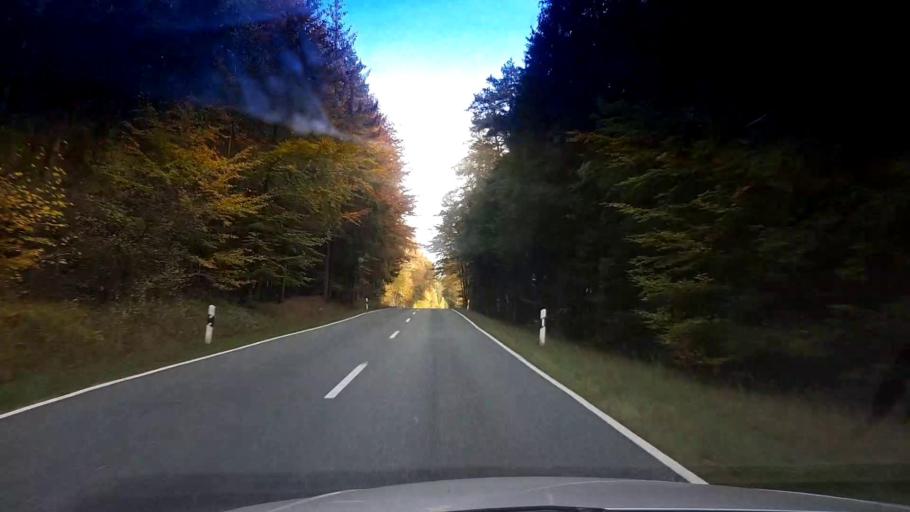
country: DE
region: Bavaria
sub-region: Upper Franconia
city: Wattendorf
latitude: 49.9962
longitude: 11.1394
